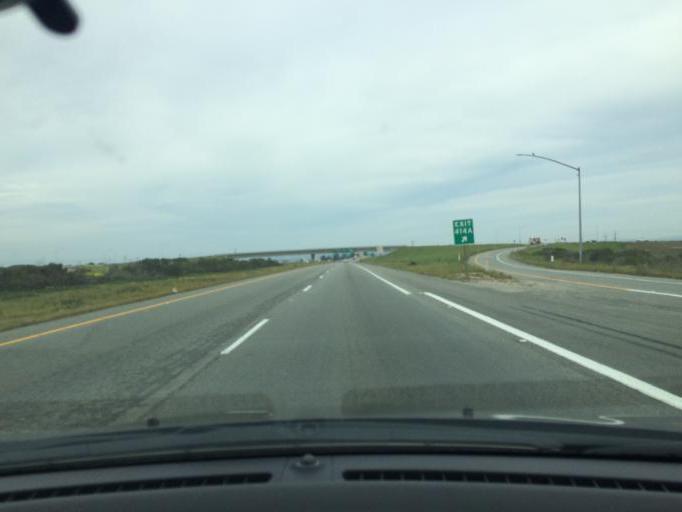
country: US
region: California
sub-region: Monterey County
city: Castroville
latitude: 36.7426
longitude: -121.7734
